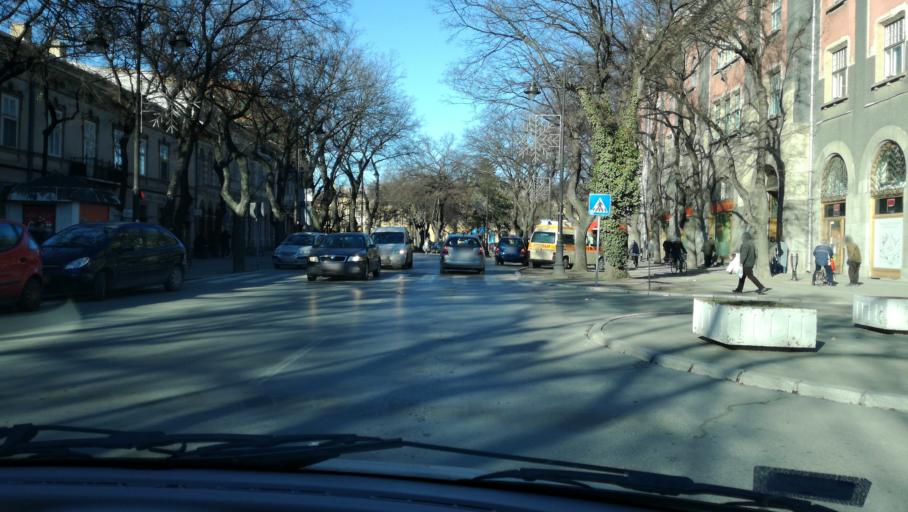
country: RS
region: Autonomna Pokrajina Vojvodina
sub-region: Severnobacki Okrug
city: Subotica
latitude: 46.0990
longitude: 19.6642
